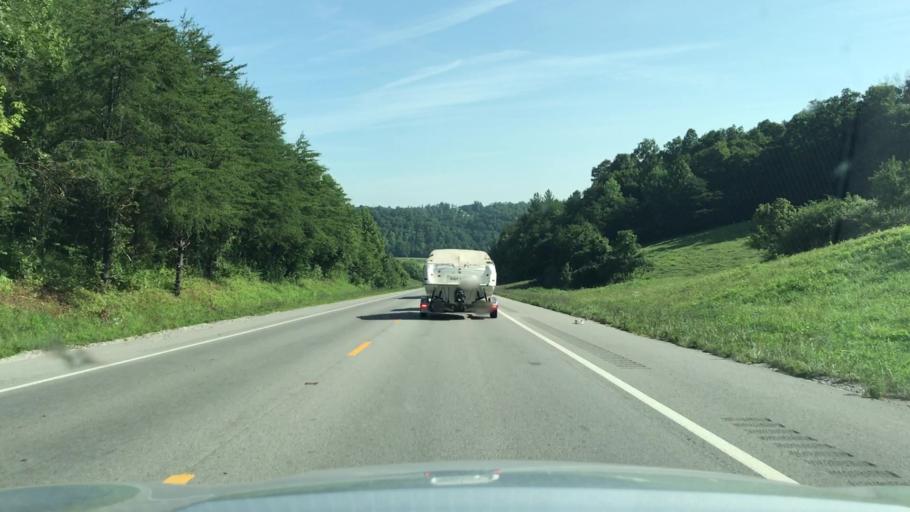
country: US
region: Tennessee
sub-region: Pickett County
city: Byrdstown
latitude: 36.5968
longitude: -85.1225
